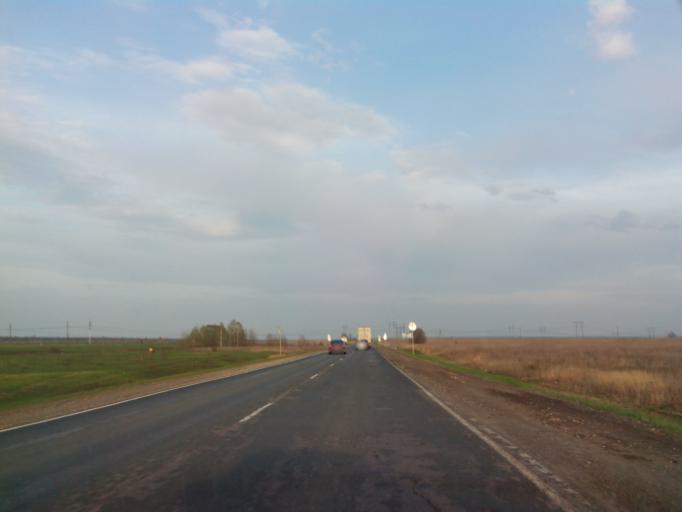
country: RU
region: Rjazan
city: Korablino
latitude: 53.7501
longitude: 39.8522
